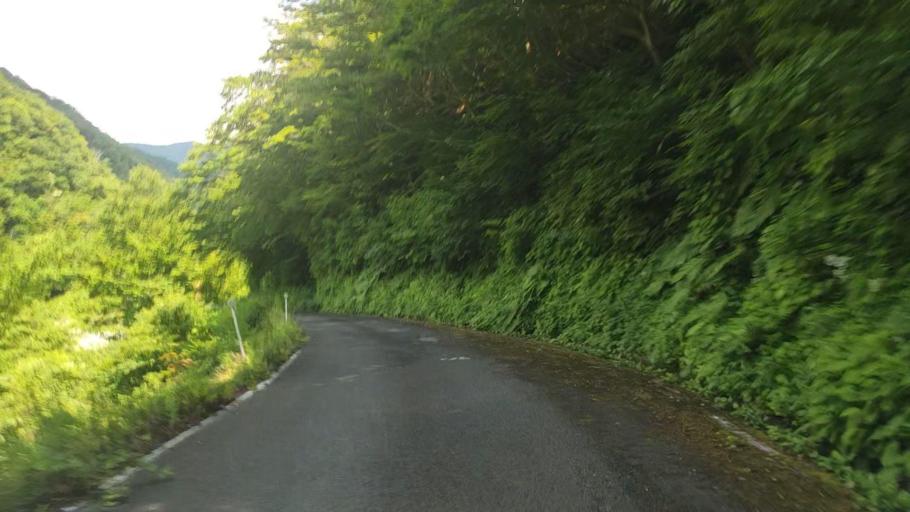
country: JP
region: Fukui
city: Ono
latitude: 35.7603
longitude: 136.5591
